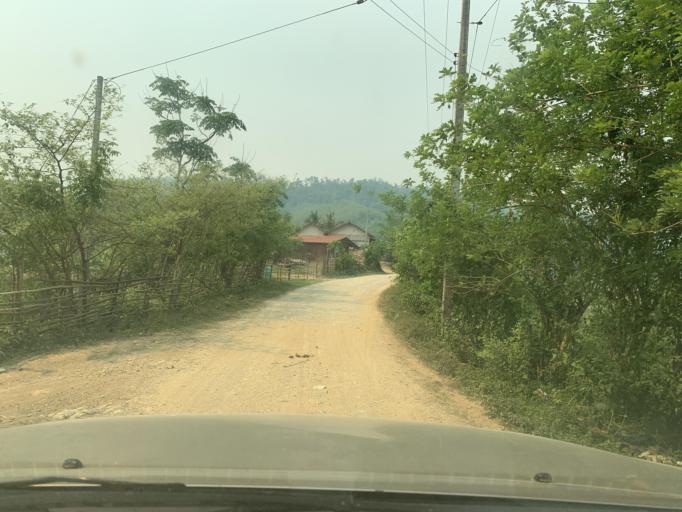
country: LA
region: Louangphabang
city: Louangphabang
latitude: 19.9003
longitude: 102.2544
